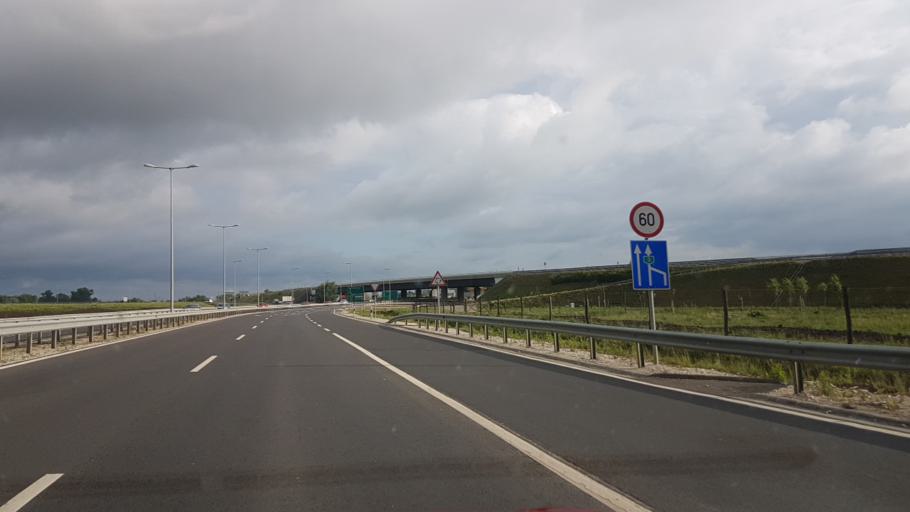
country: HU
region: Borsod-Abauj-Zemplen
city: Arnot
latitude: 48.1111
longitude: 20.8448
